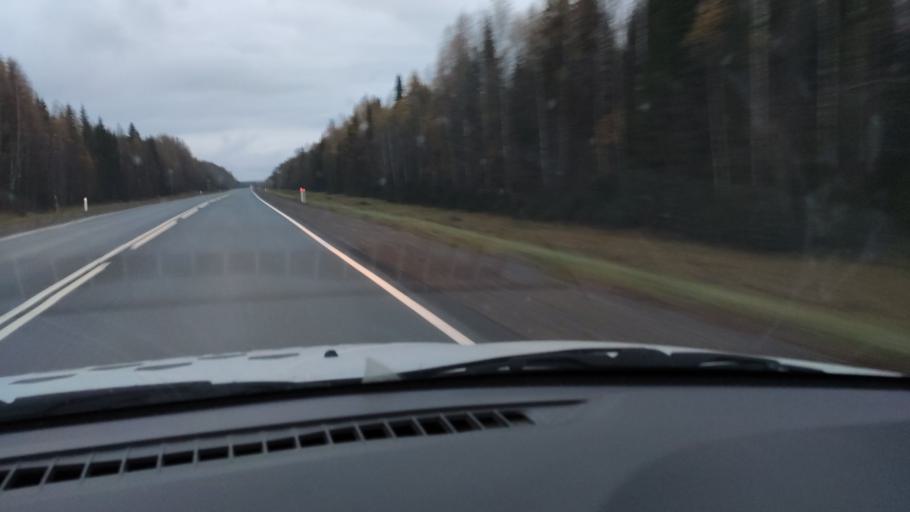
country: RU
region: Kirov
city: Kostino
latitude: 58.8587
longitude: 53.1071
